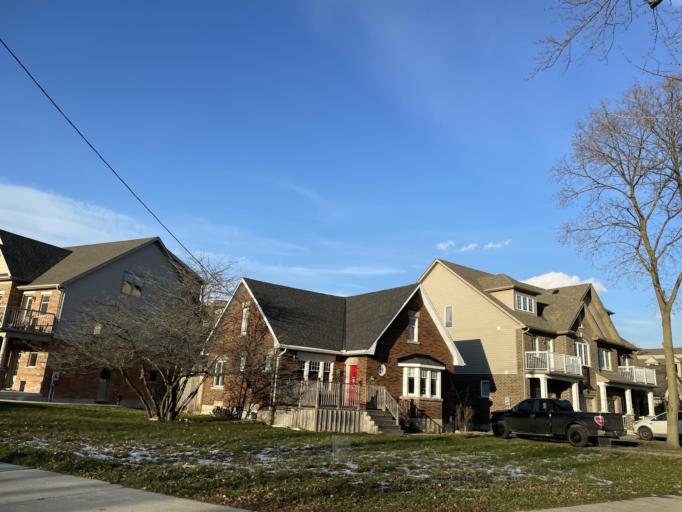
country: CA
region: Ontario
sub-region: Wellington County
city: Guelph
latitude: 43.5413
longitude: -80.2406
